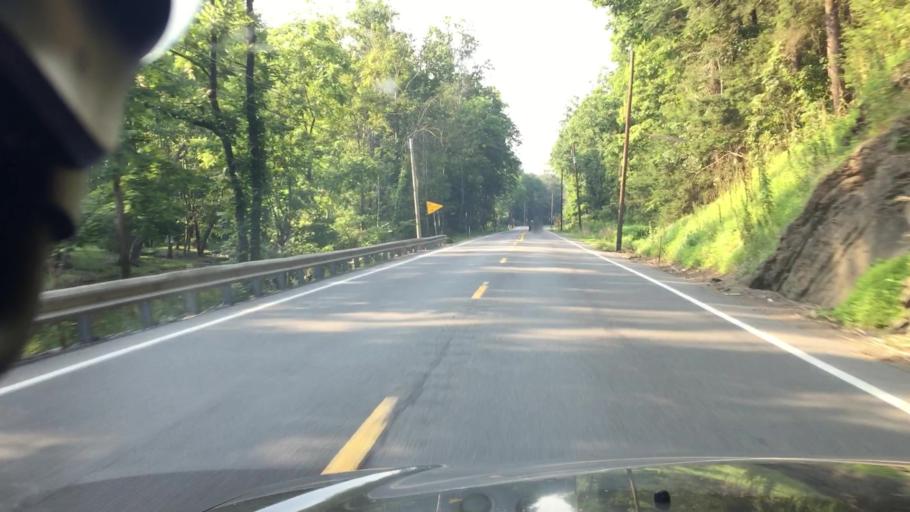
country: US
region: Pennsylvania
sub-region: Northumberland County
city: Elysburg
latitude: 40.8980
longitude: -76.5103
